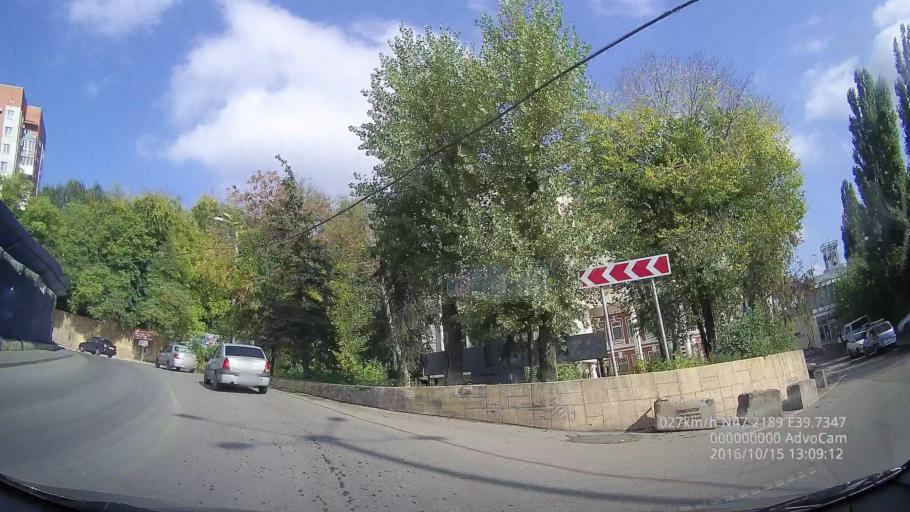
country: RU
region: Rostov
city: Rostov-na-Donu
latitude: 47.2194
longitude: 39.7345
